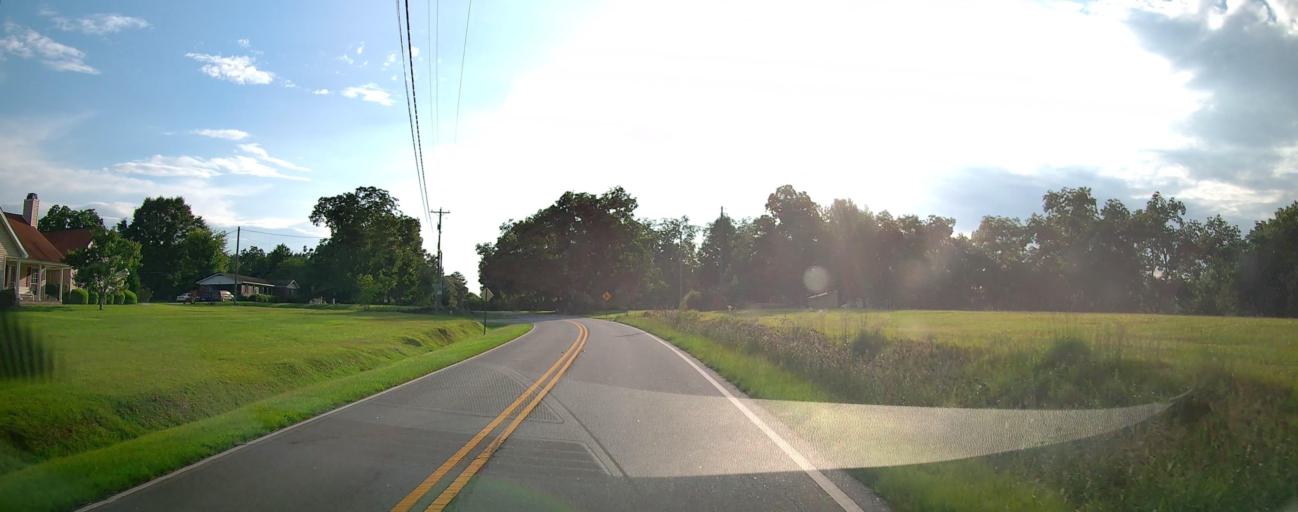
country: US
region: Georgia
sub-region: Peach County
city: Byron
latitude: 32.7289
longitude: -83.7461
